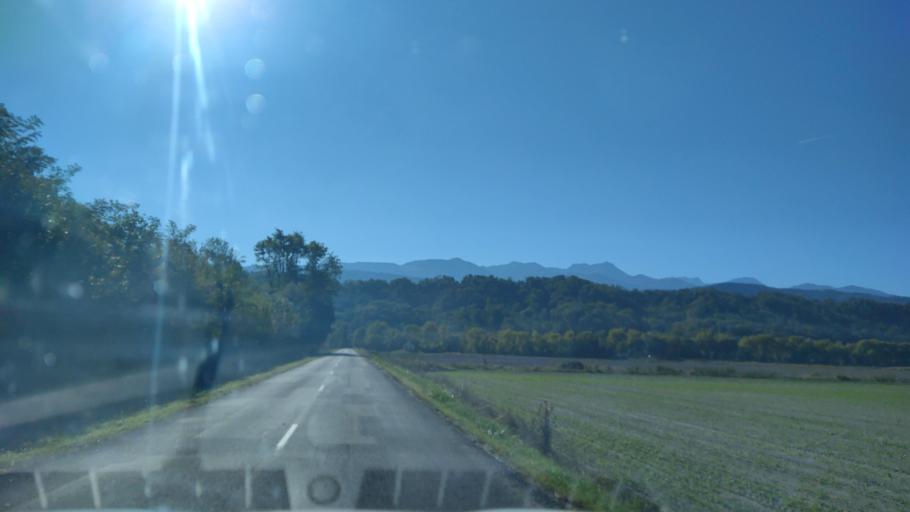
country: FR
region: Rhone-Alpes
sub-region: Departement de la Savoie
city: Coise-Saint-Jean-Pied-Gauthier
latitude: 45.5454
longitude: 6.1315
